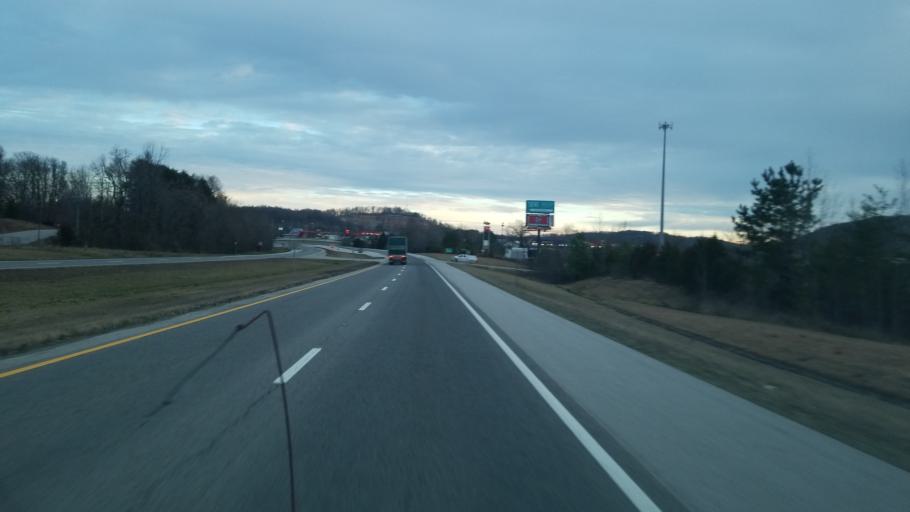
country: US
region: Tennessee
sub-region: Putnam County
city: Cookeville
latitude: 36.1264
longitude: -85.4831
